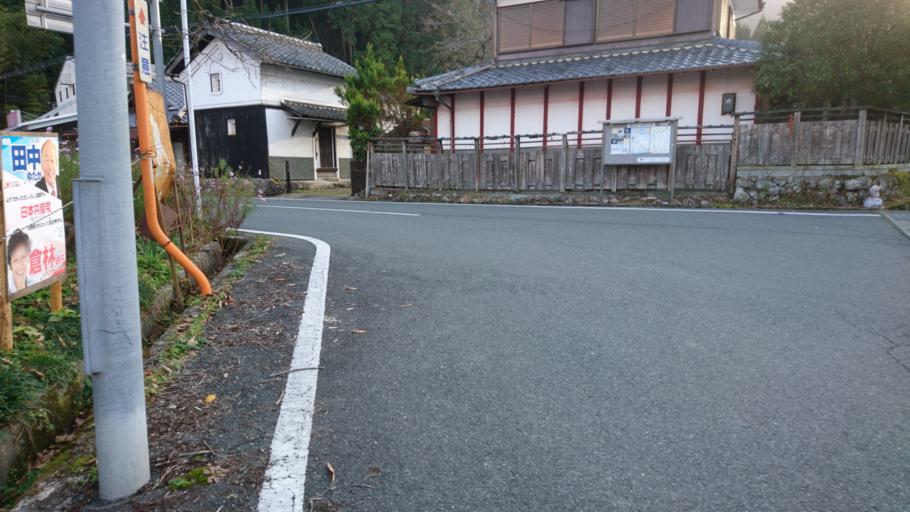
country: JP
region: Kyoto
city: Kameoka
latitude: 35.0484
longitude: 135.4702
